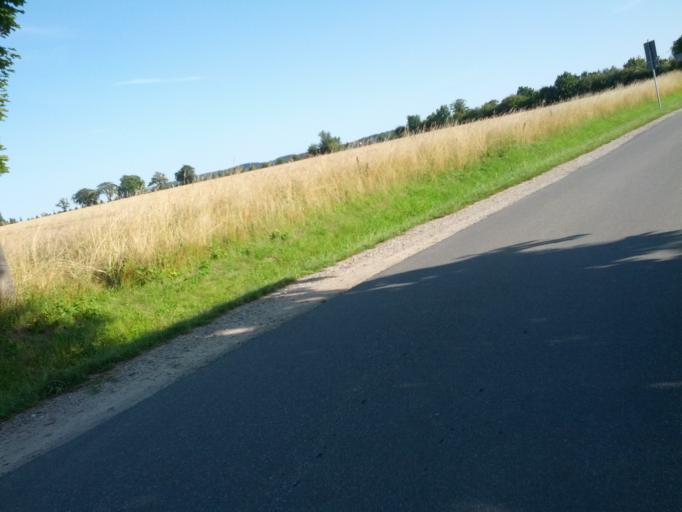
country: DE
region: Mecklenburg-Vorpommern
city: Bastorf
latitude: 54.1433
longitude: 11.7116
